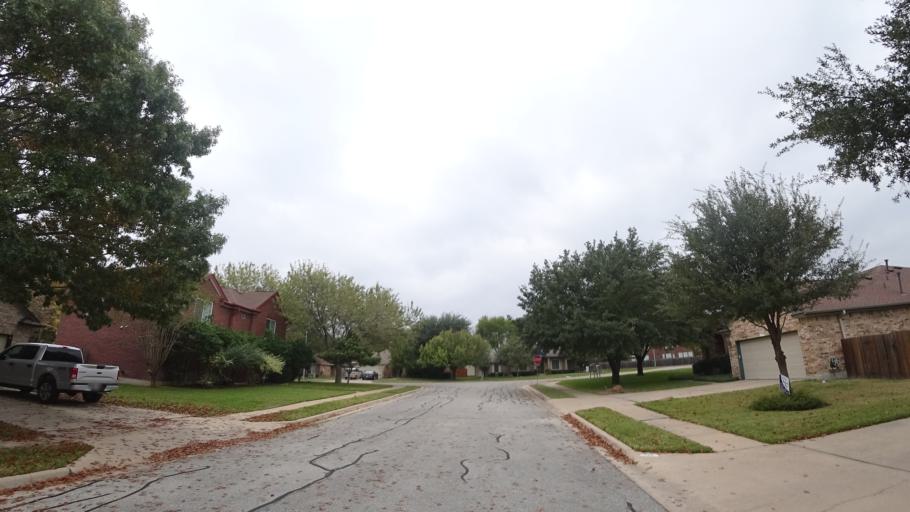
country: US
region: Texas
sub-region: Travis County
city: Pflugerville
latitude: 30.4456
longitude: -97.6091
